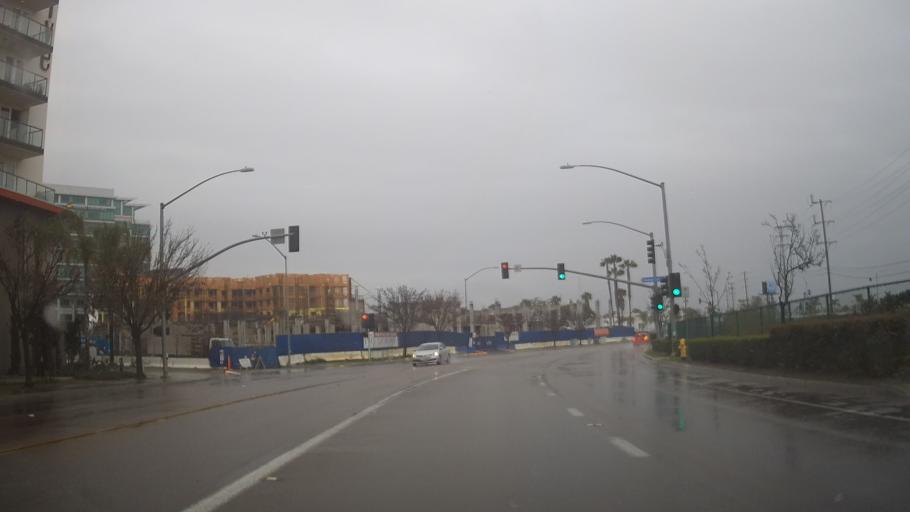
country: US
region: California
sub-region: San Diego County
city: San Diego
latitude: 32.8290
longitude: -117.1404
